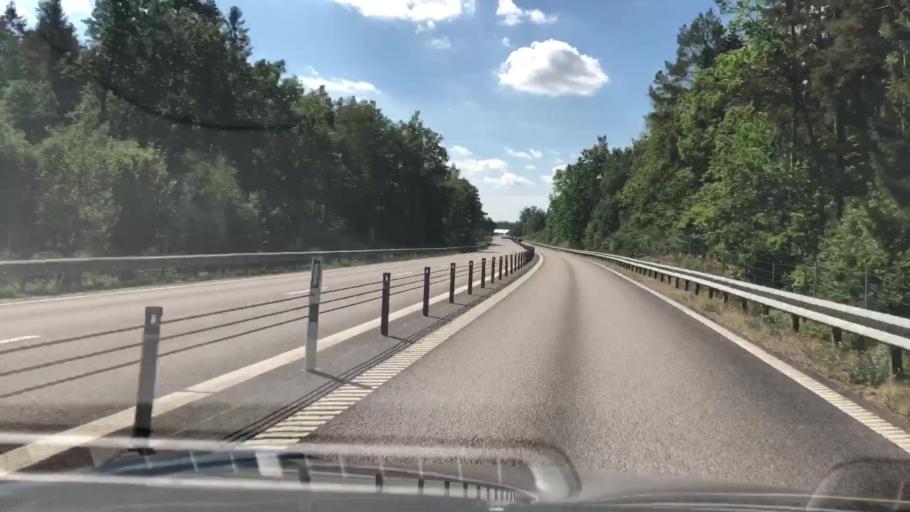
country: SE
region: Kalmar
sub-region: Monsteras Kommun
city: Timmernabben
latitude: 56.8601
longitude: 16.3789
